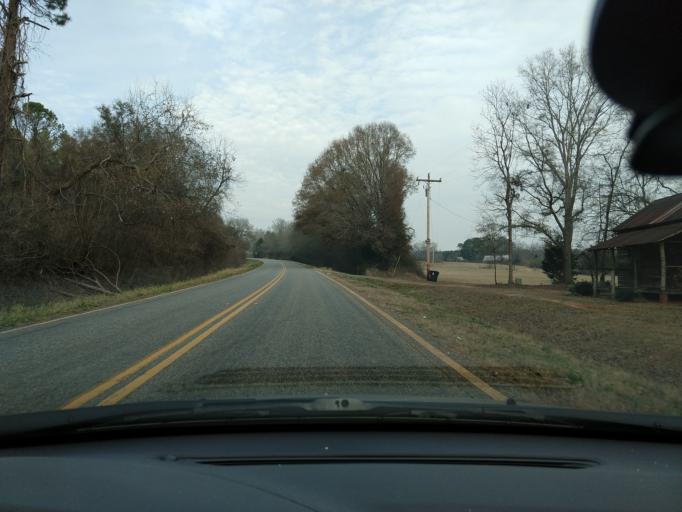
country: US
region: Georgia
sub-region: Webster County
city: Preston
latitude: 32.0144
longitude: -84.4087
